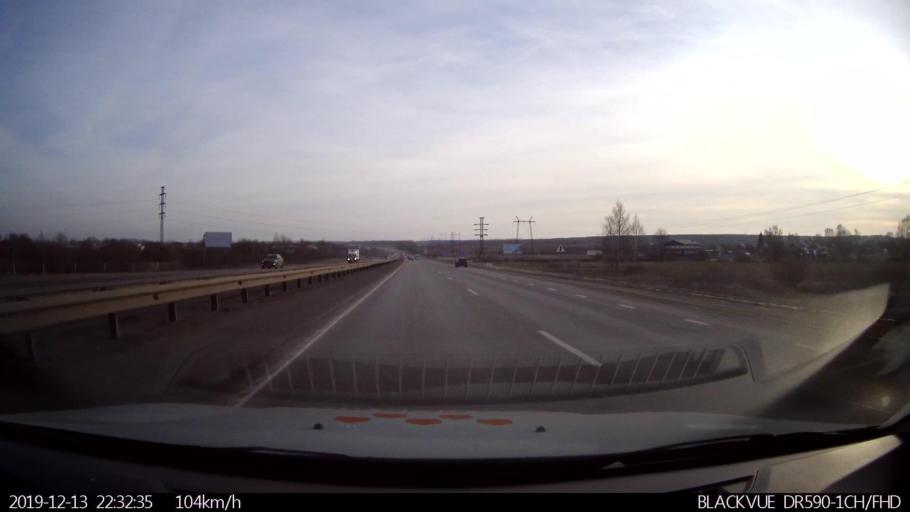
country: RU
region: Nizjnij Novgorod
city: Afonino
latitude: 56.2041
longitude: 44.0946
